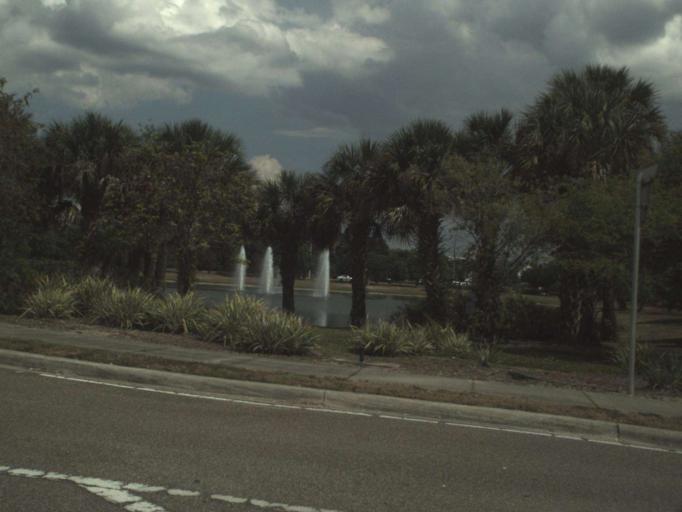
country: US
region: Florida
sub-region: Lake County
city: Tavares
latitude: 28.8098
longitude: -81.7362
